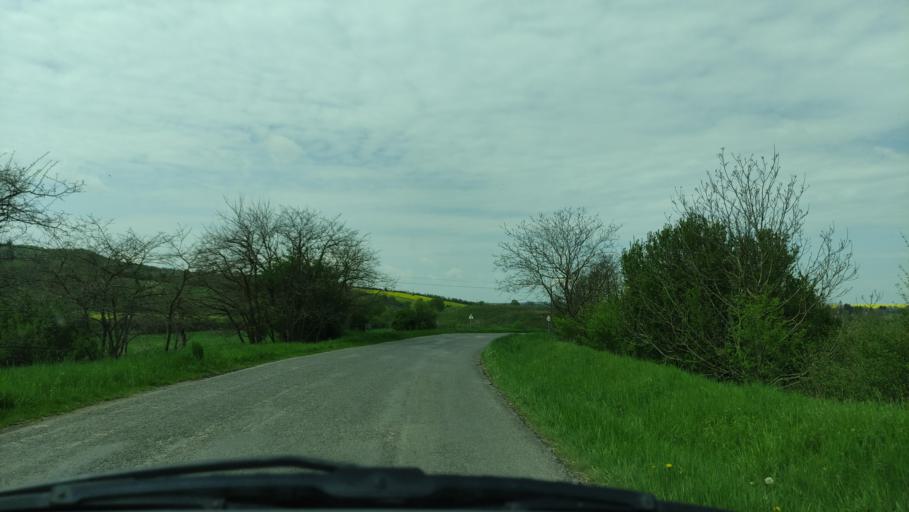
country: HU
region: Baranya
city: Sasd
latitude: 46.3055
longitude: 18.1526
